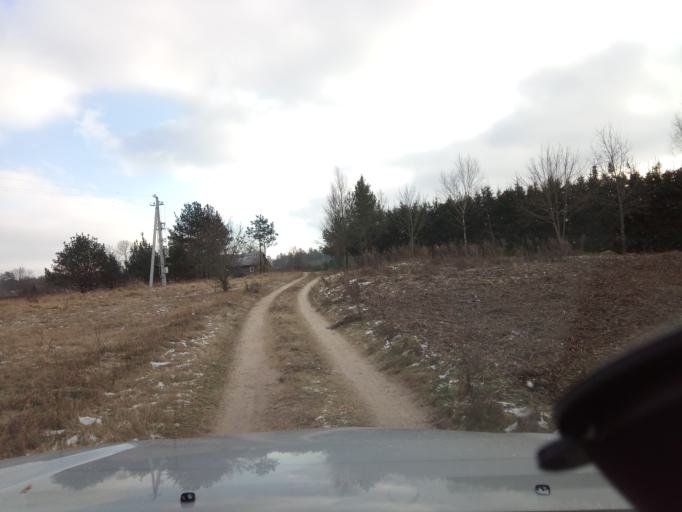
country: LT
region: Alytaus apskritis
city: Druskininkai
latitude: 54.1125
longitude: 24.2195
